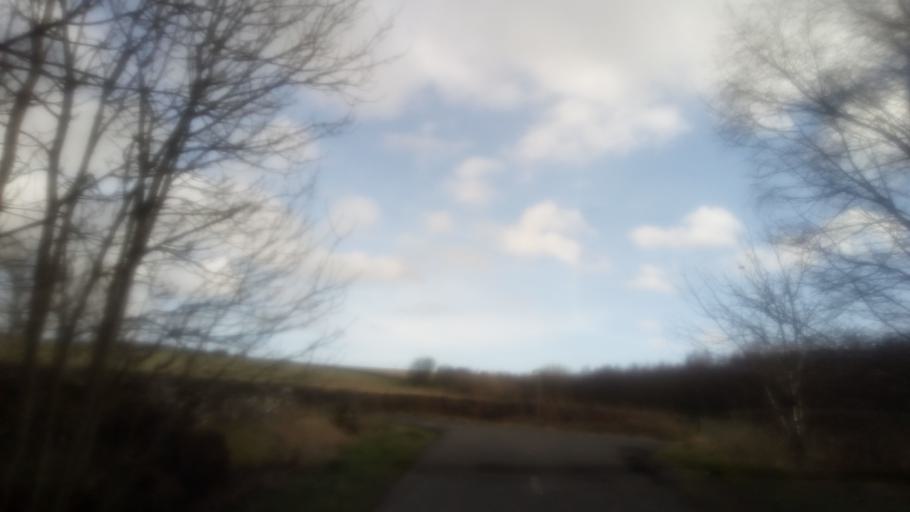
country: GB
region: Scotland
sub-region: The Scottish Borders
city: Jedburgh
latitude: 55.4690
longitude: -2.6067
